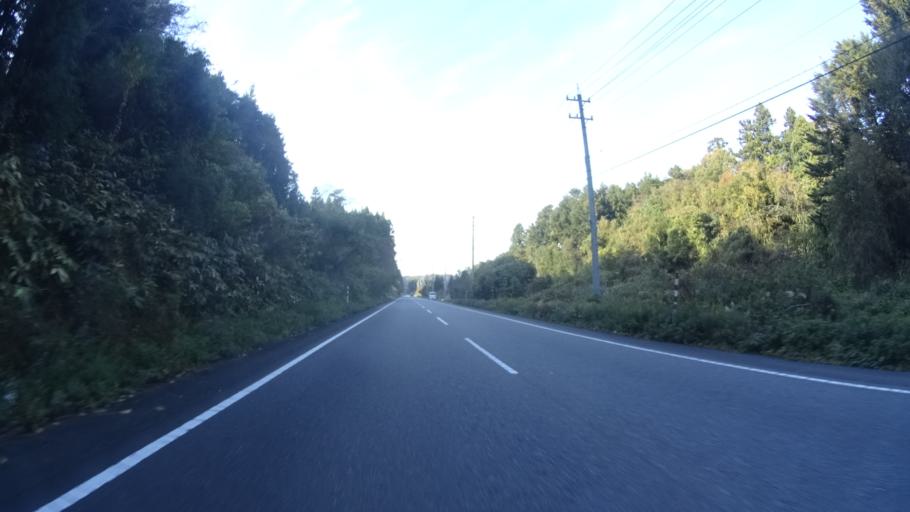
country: JP
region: Ishikawa
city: Hakui
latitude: 37.0119
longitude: 136.7982
